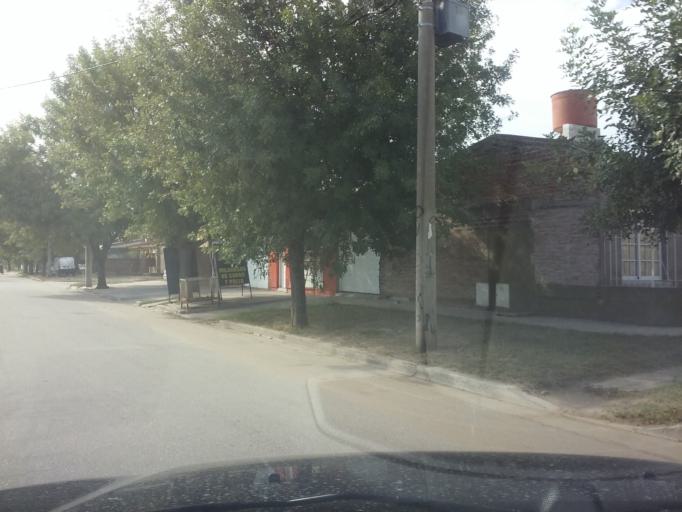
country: AR
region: La Pampa
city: Santa Rosa
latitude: -36.6495
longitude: -64.2942
